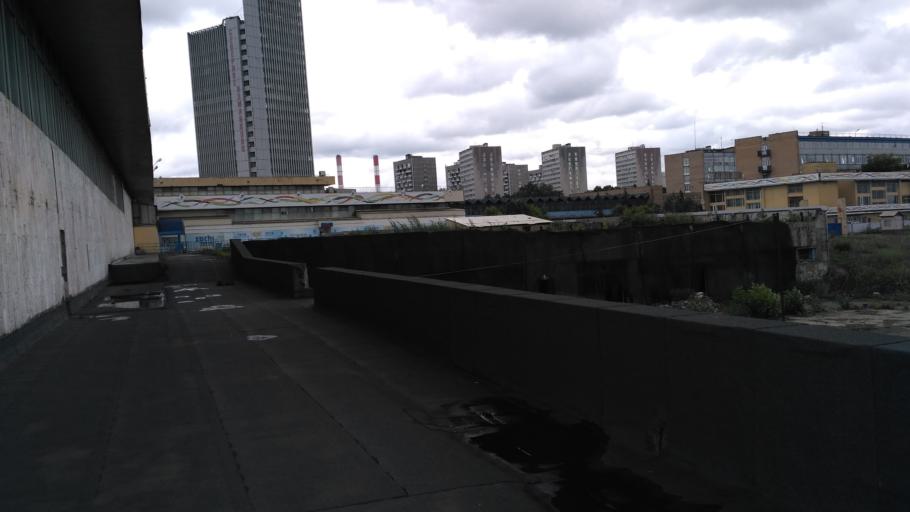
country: RU
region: Moscow
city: Metrogorodok
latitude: 55.7994
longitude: 37.7558
